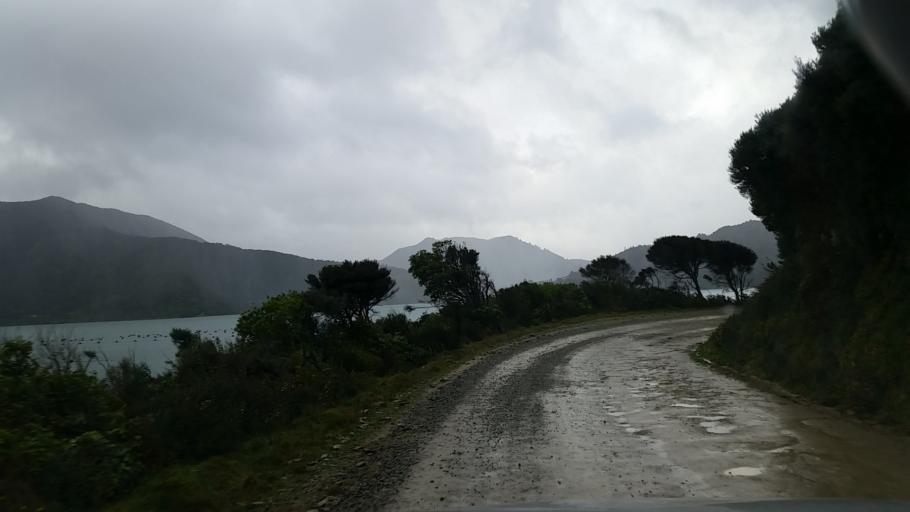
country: NZ
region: Marlborough
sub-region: Marlborough District
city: Picton
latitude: -41.1764
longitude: 174.0472
